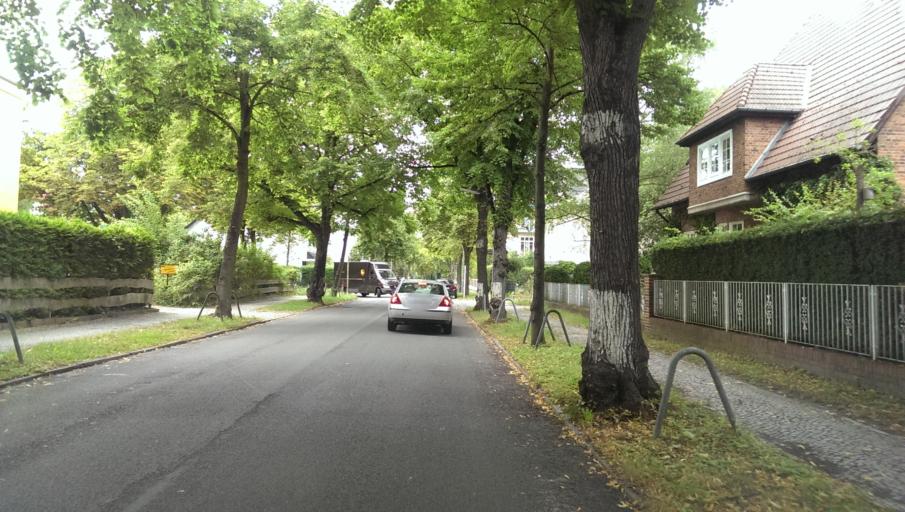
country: DE
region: Berlin
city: Lankwitz
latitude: 52.4348
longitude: 13.3340
